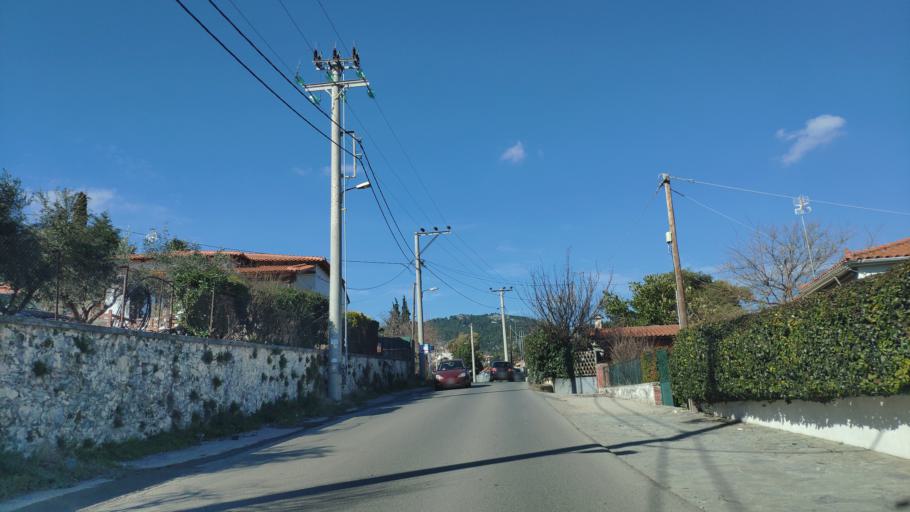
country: GR
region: Attica
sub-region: Nomarchia Anatolikis Attikis
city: Afidnes
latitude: 38.1979
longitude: 23.8420
